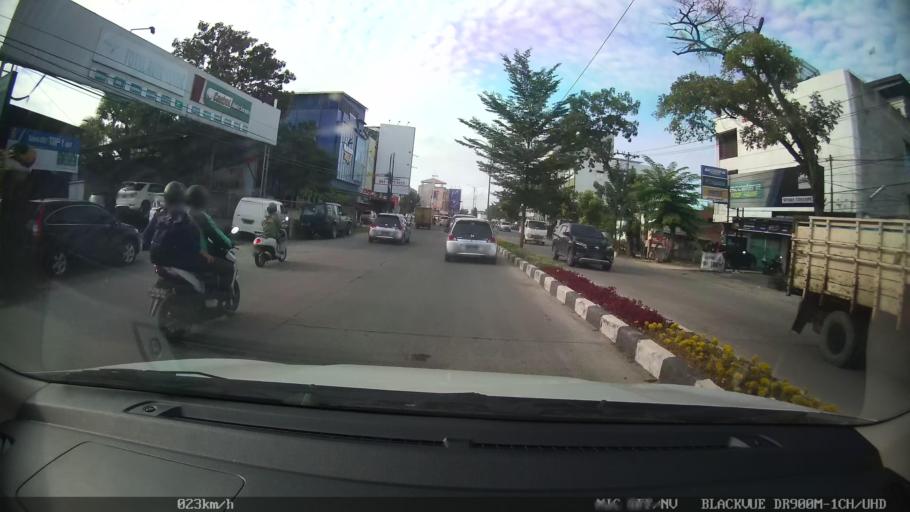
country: ID
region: North Sumatra
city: Medan
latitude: 3.6285
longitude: 98.6810
